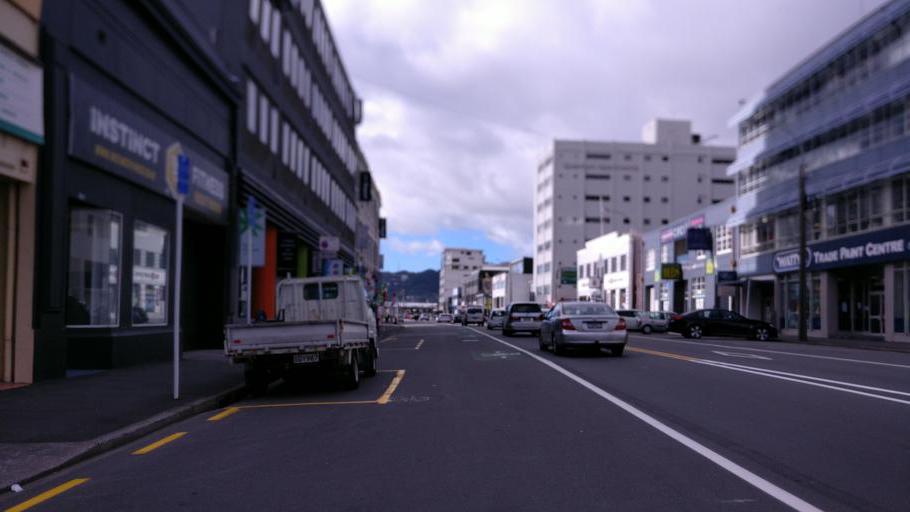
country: NZ
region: Wellington
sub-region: Wellington City
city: Wellington
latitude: -41.2718
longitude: 174.7821
